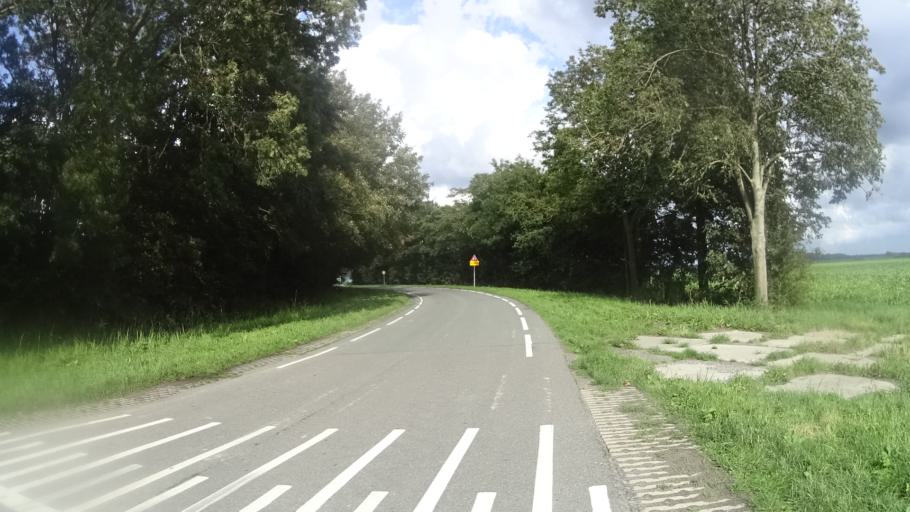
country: NL
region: North Holland
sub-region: Gemeente Hollands Kroon
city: Den Oever
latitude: 52.8650
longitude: 4.9289
